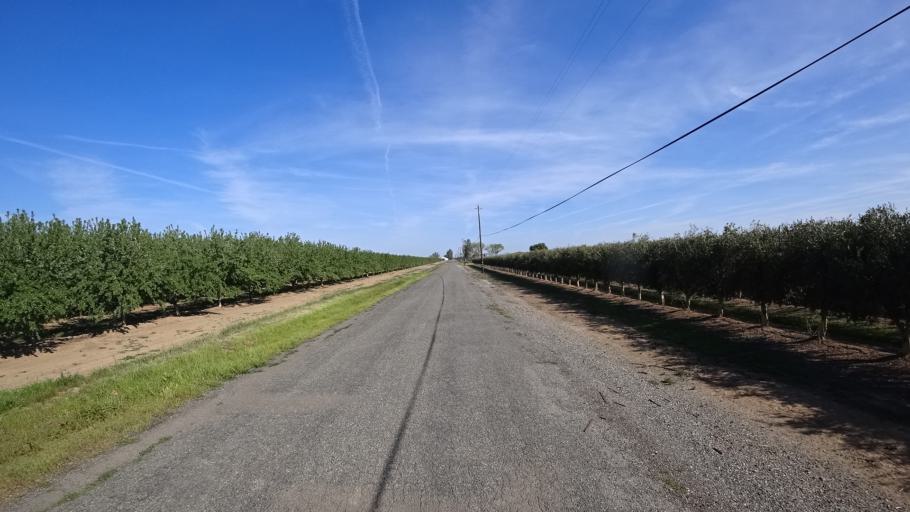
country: US
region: California
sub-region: Glenn County
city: Willows
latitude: 39.6287
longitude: -122.2160
